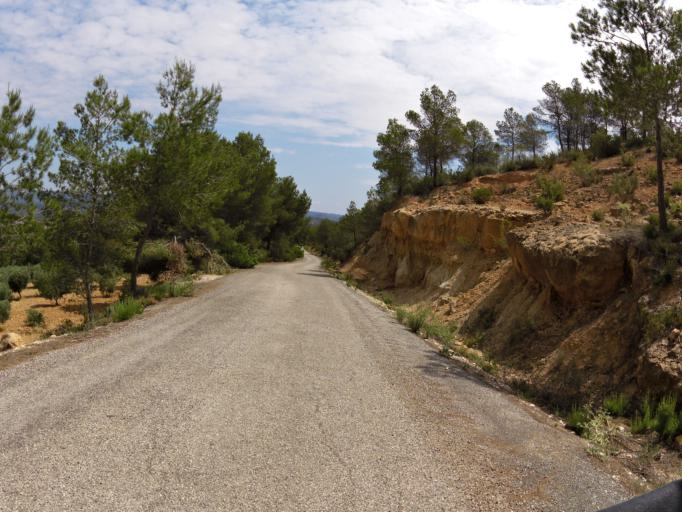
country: ES
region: Castille-La Mancha
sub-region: Provincia de Albacete
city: Casas Ibanez
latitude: 39.3637
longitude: -1.4644
